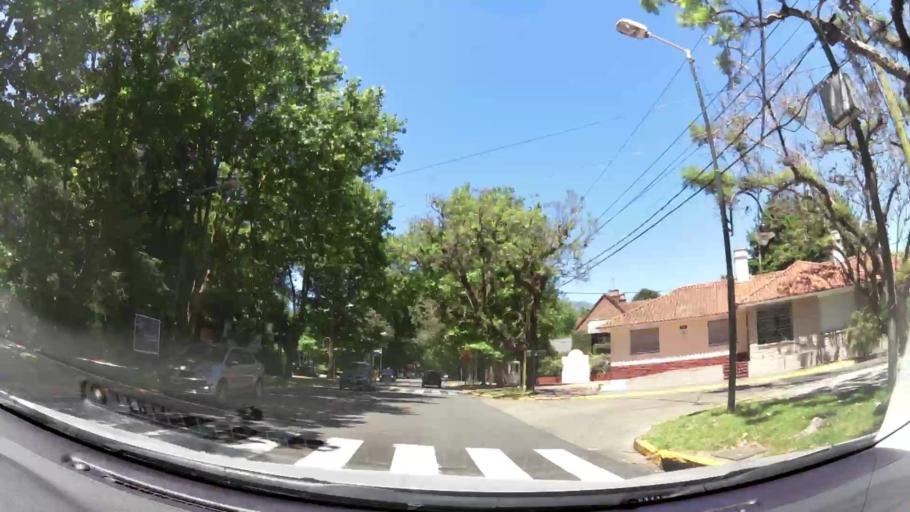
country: AR
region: Buenos Aires
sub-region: Partido de San Isidro
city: San Isidro
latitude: -34.4480
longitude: -58.5384
